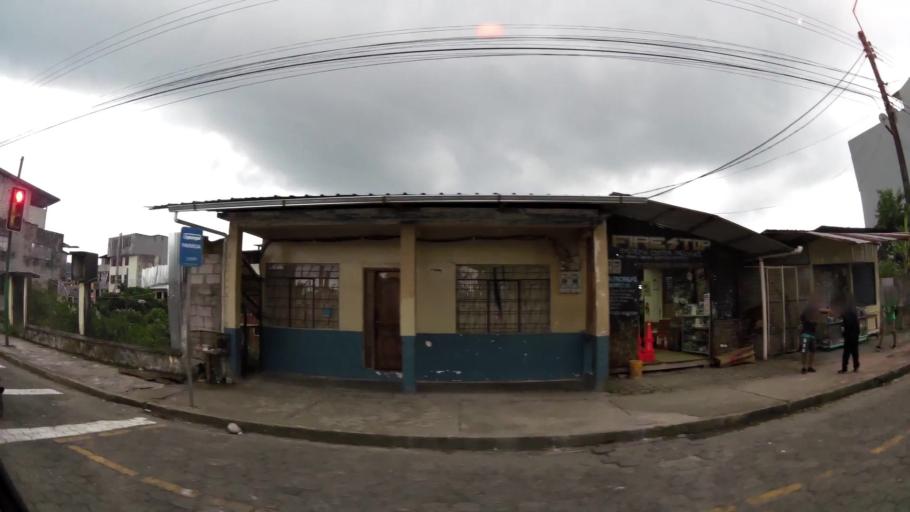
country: EC
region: Pastaza
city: Puyo
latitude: -1.4865
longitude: -78.0027
